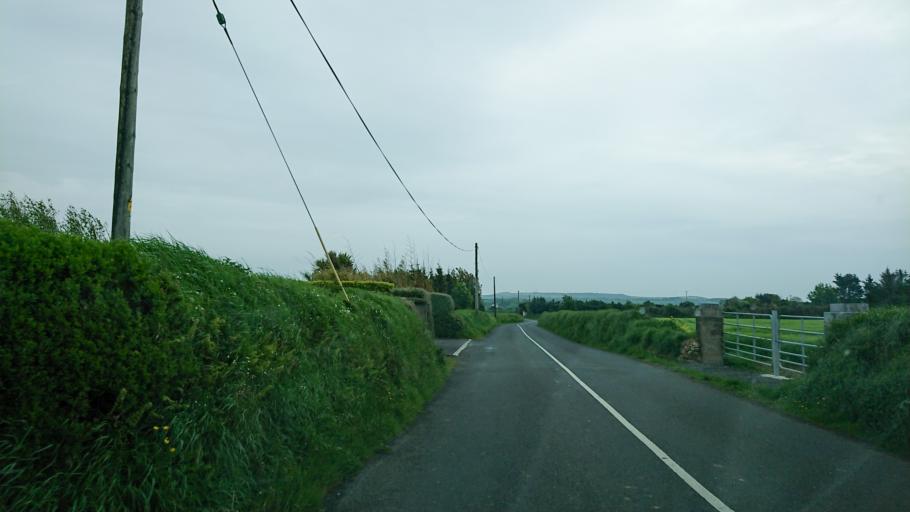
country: IE
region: Munster
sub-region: Waterford
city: Waterford
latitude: 52.2233
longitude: -7.0535
